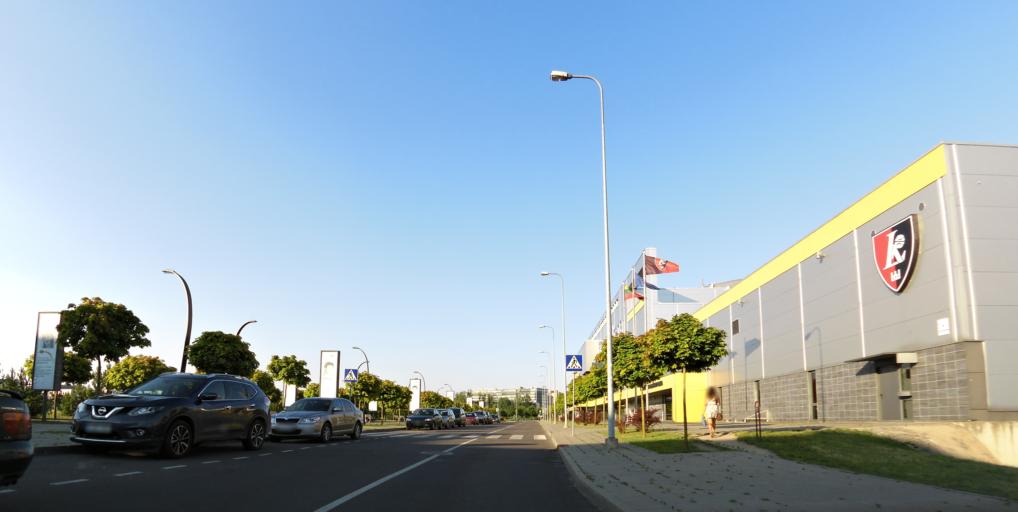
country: LT
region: Vilnius County
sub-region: Vilnius
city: Vilnius
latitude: 54.7159
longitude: 25.2780
